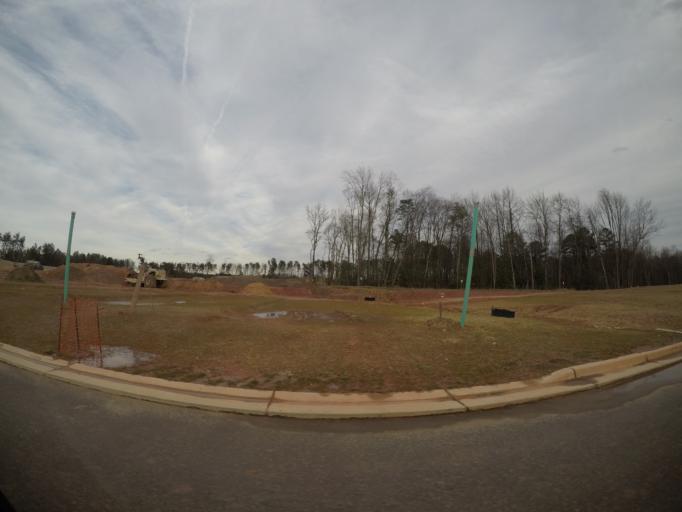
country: US
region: Maryland
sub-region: Anne Arundel County
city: Odenton
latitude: 39.0993
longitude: -76.7050
